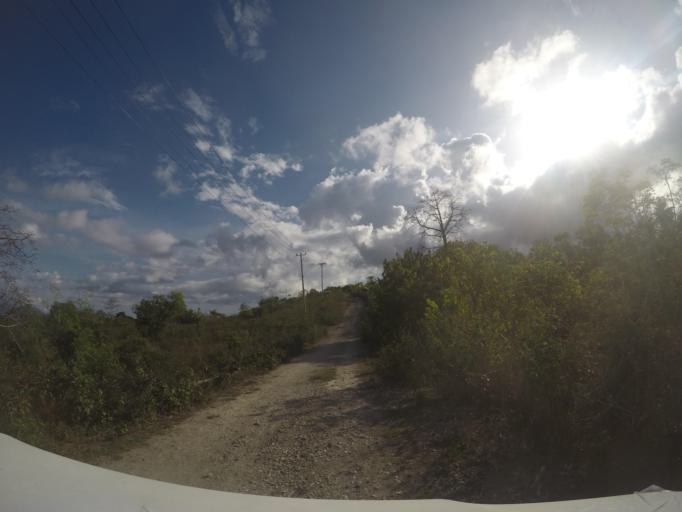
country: TL
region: Baucau
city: Baucau
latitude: -8.4733
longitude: 126.4642
